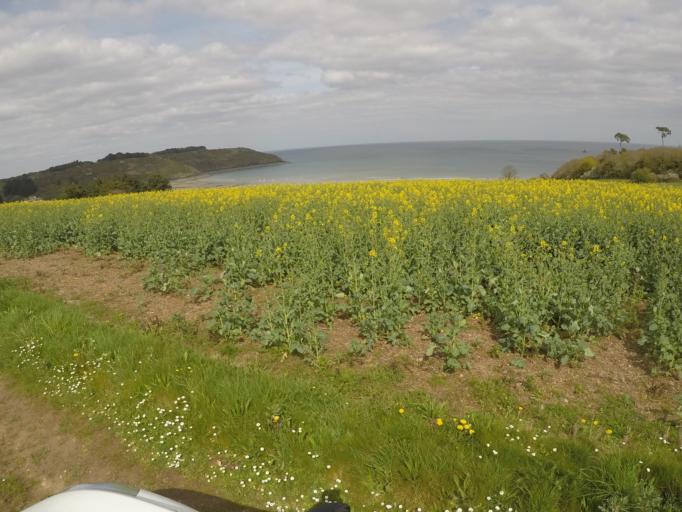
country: FR
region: Brittany
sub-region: Departement des Cotes-d'Armor
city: Plouha
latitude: 48.7186
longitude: -2.9456
